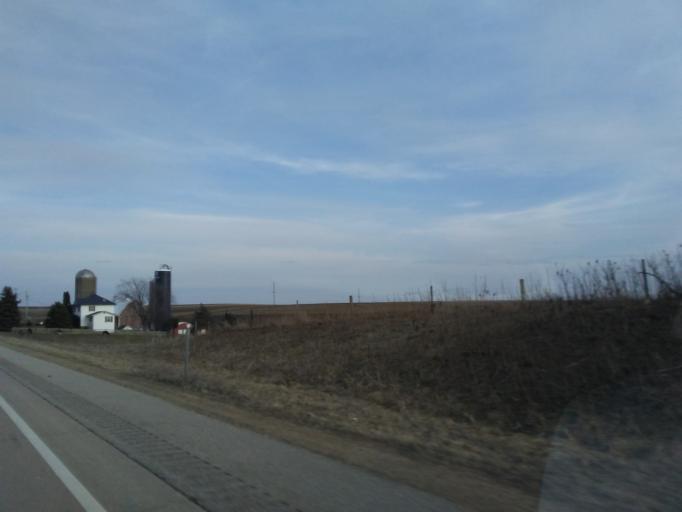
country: US
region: Wisconsin
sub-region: Iowa County
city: Barneveld
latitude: 43.0094
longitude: -89.9427
